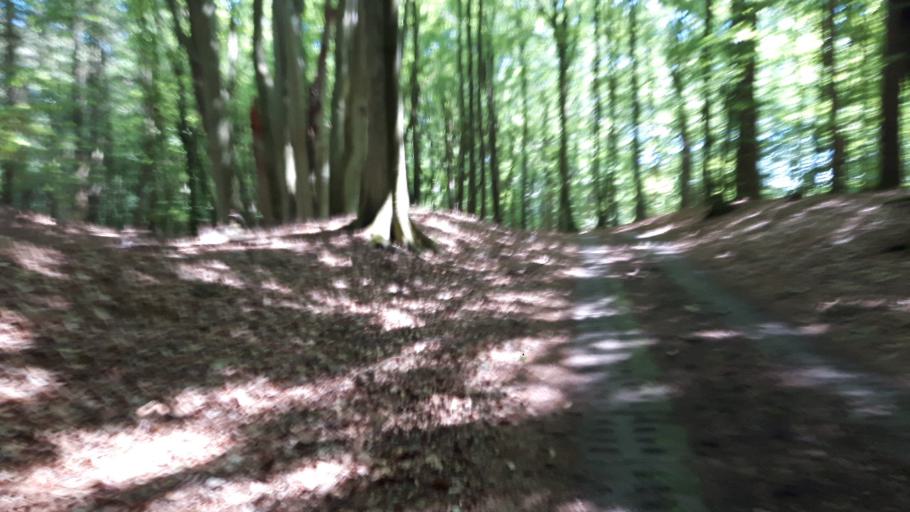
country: PL
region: Pomeranian Voivodeship
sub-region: Powiat slupski
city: Smoldzino
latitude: 54.6713
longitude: 17.1797
